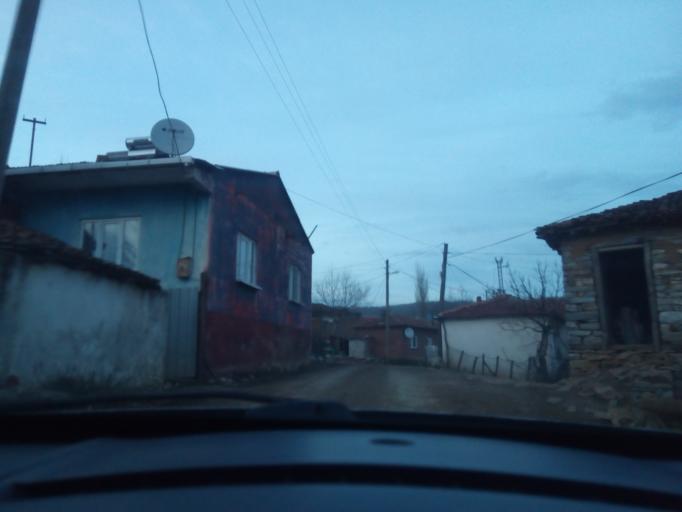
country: TR
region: Balikesir
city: Omerkoy
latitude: 39.9096
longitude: 28.0369
